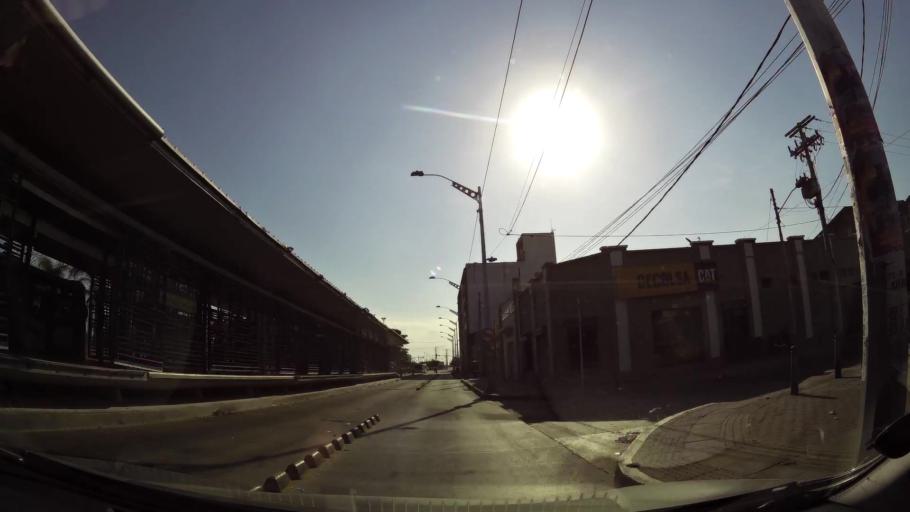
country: CO
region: Atlantico
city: Barranquilla
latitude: 10.9859
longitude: -74.7787
